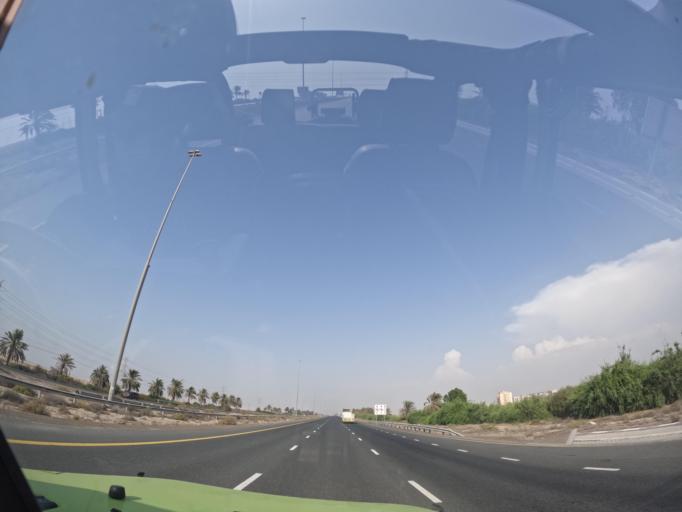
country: AE
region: Dubai
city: Dubai
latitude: 24.8717
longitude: 55.0293
